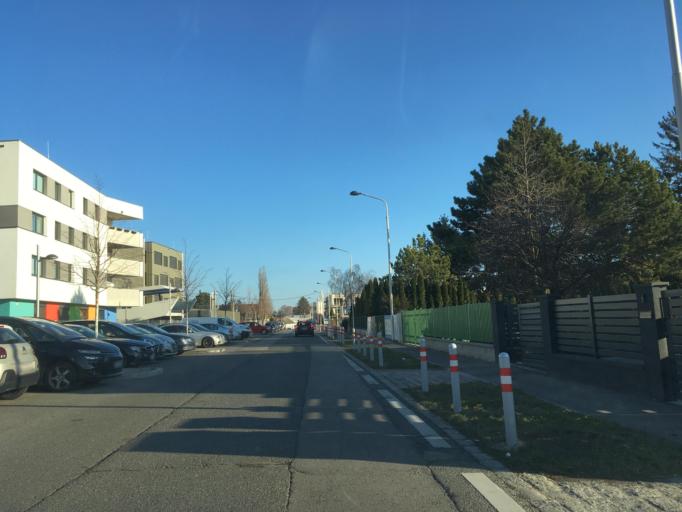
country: AT
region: Lower Austria
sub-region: Politischer Bezirk Wien-Umgebung
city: Leopoldsdorf
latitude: 48.1395
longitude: 16.3959
